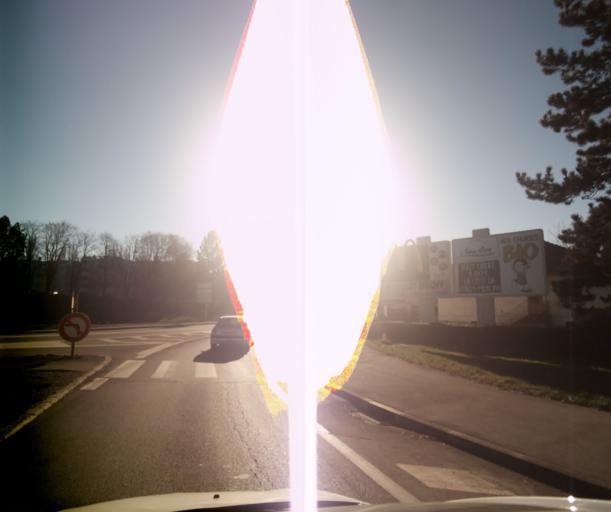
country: FR
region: Franche-Comte
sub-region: Departement du Doubs
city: Avanne-Aveney
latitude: 47.2267
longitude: 5.9783
